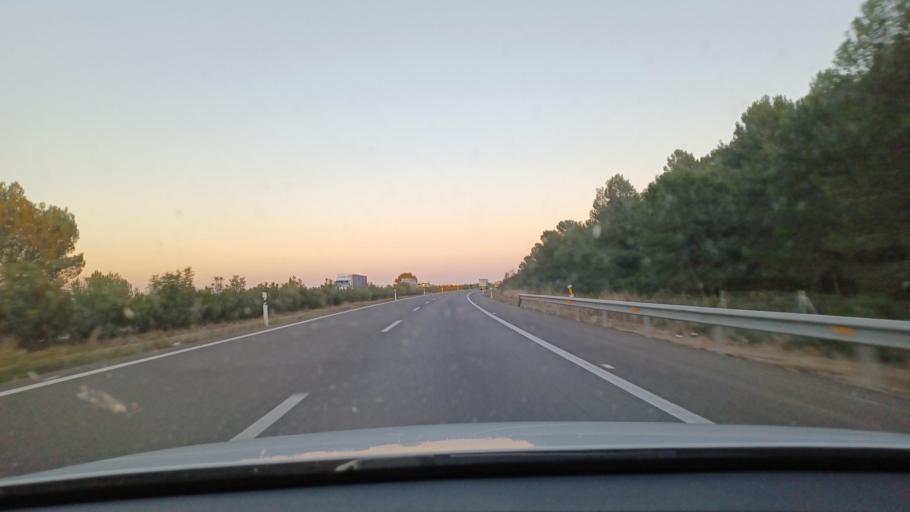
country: ES
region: Valencia
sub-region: Provincia de Castello
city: Santa Magdalena de Pulpis
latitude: 40.3908
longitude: 0.3541
